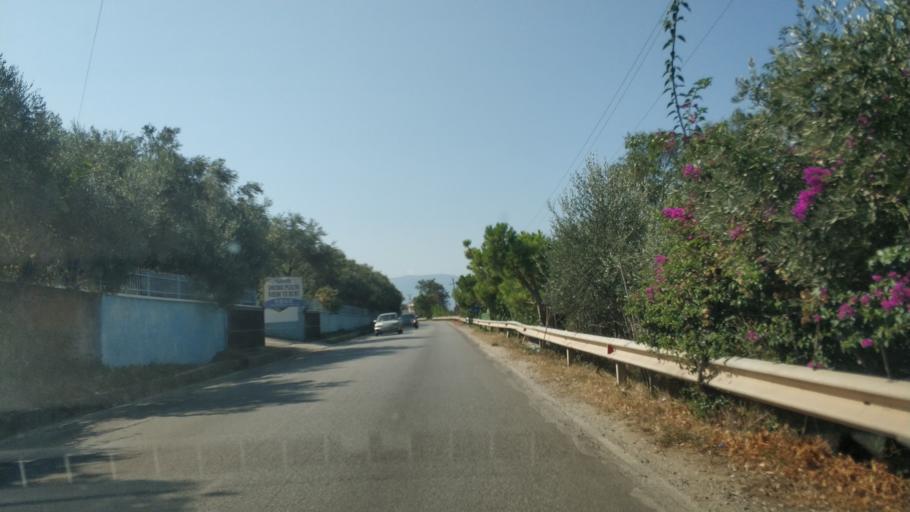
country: AL
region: Vlore
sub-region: Rrethi i Vlores
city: Orikum
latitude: 40.3802
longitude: 19.4826
